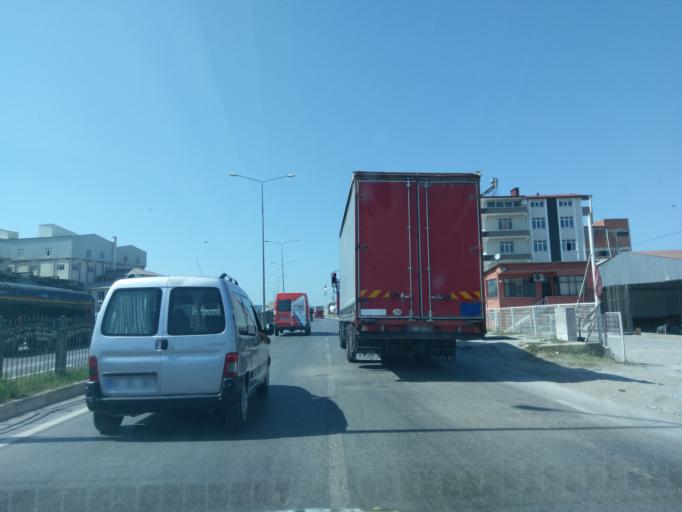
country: TR
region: Samsun
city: Bafra
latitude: 41.5650
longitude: 35.8862
